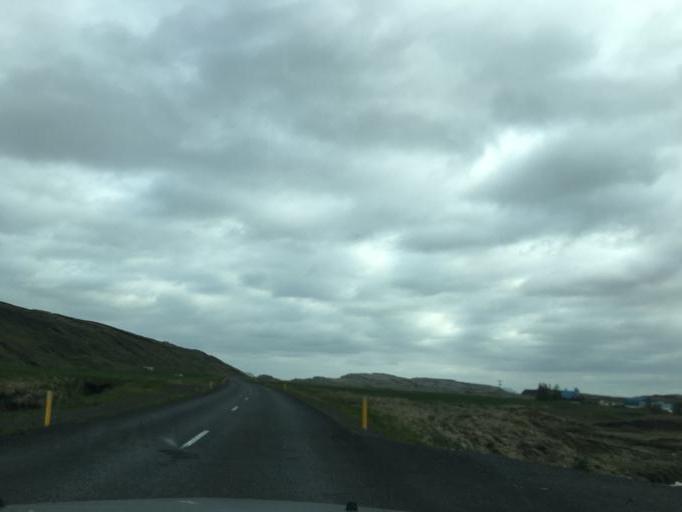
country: IS
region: South
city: Vestmannaeyjar
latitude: 64.2225
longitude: -20.2579
